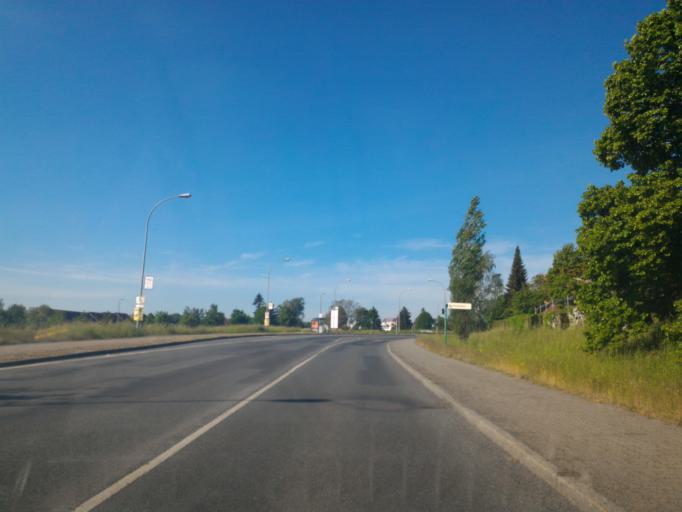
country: DE
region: Saxony
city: Lobau
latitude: 51.0869
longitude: 14.6684
